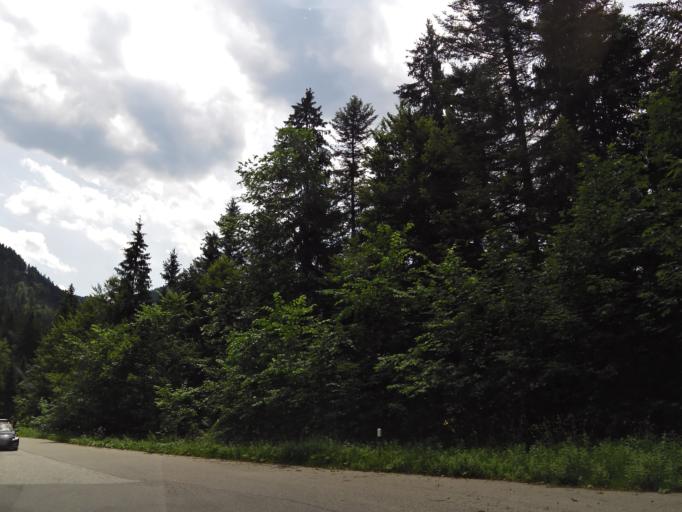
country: AT
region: Tyrol
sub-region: Politischer Bezirk Kitzbuhel
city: Waidring
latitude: 47.6586
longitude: 12.5465
